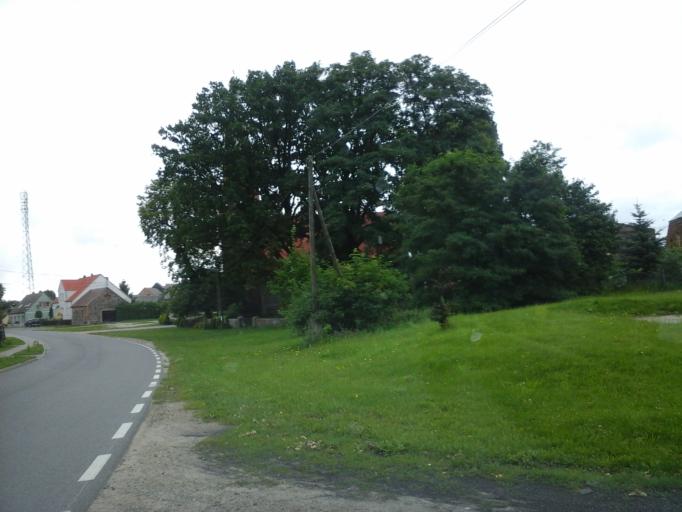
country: PL
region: West Pomeranian Voivodeship
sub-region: Powiat choszczenski
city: Krzecin
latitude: 53.0032
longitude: 15.4230
